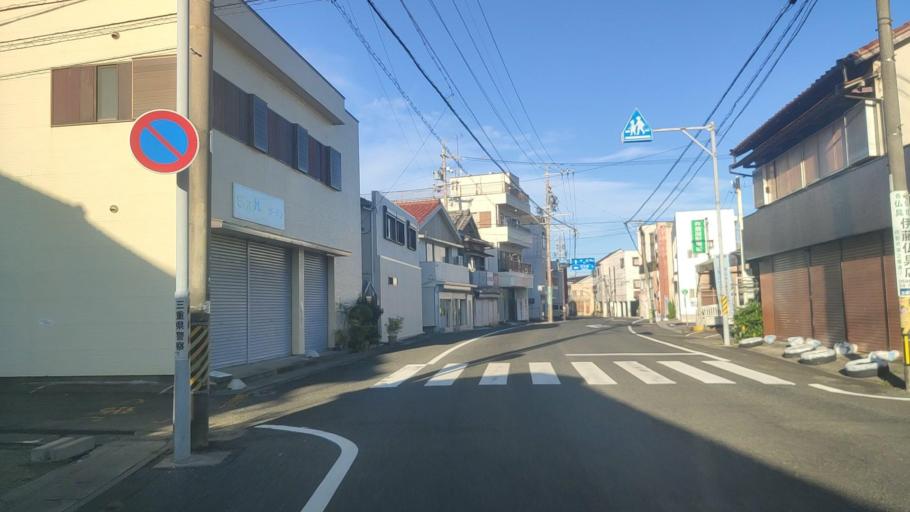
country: JP
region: Mie
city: Toba
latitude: 34.2563
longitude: 136.8067
